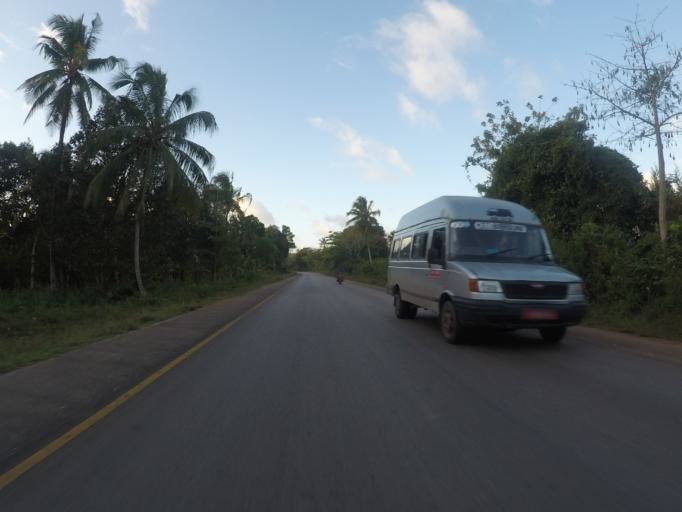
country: TZ
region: Zanzibar Central/South
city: Koani
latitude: -6.1735
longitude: 39.3295
